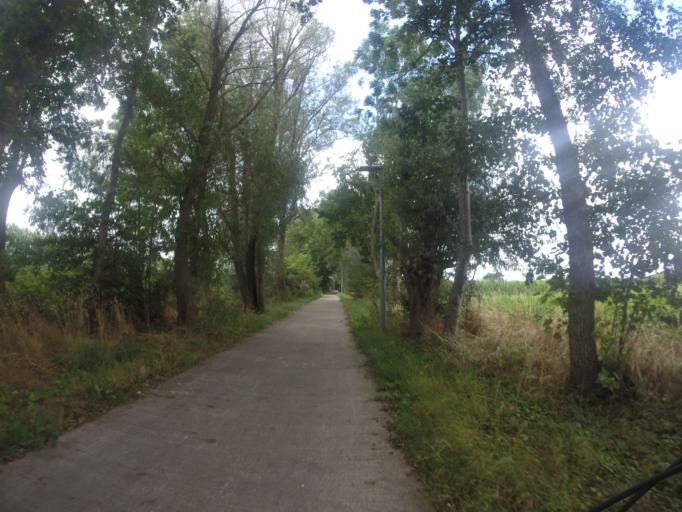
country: BE
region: Flanders
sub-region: Provincie West-Vlaanderen
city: Roeselare
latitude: 50.9261
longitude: 3.1033
